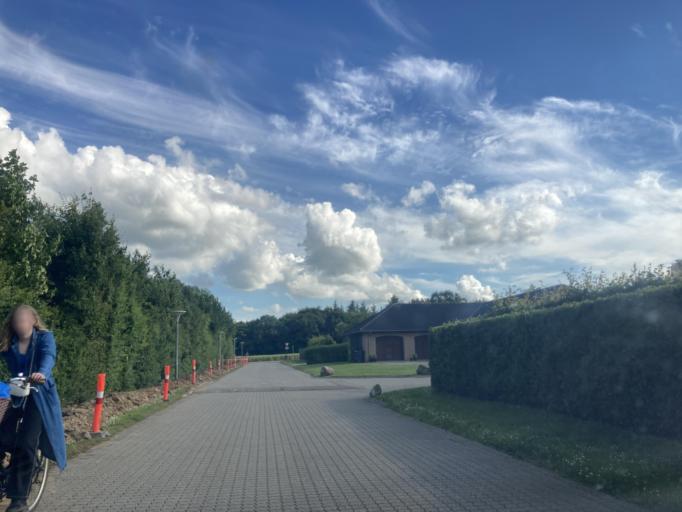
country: DK
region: South Denmark
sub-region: Vejen Kommune
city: Vejen
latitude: 55.4709
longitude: 9.1092
